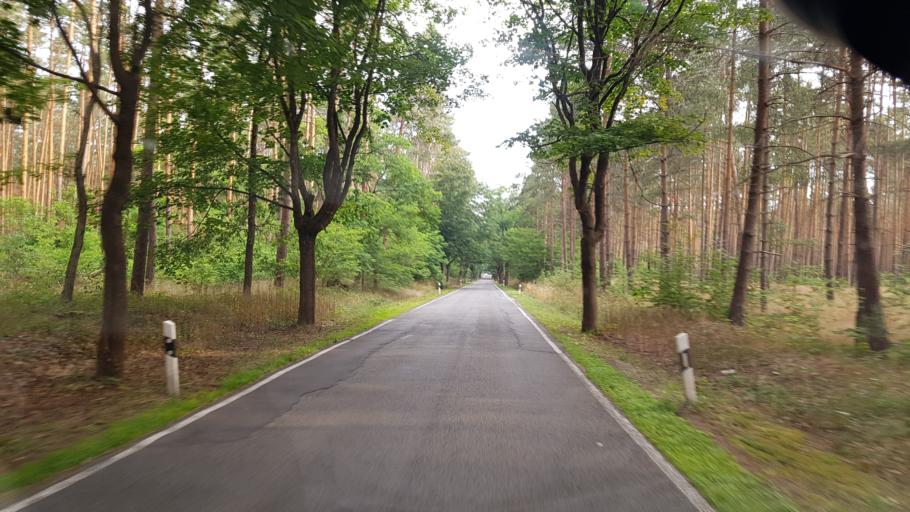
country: DE
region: Brandenburg
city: Dahme
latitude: 51.9290
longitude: 13.3973
